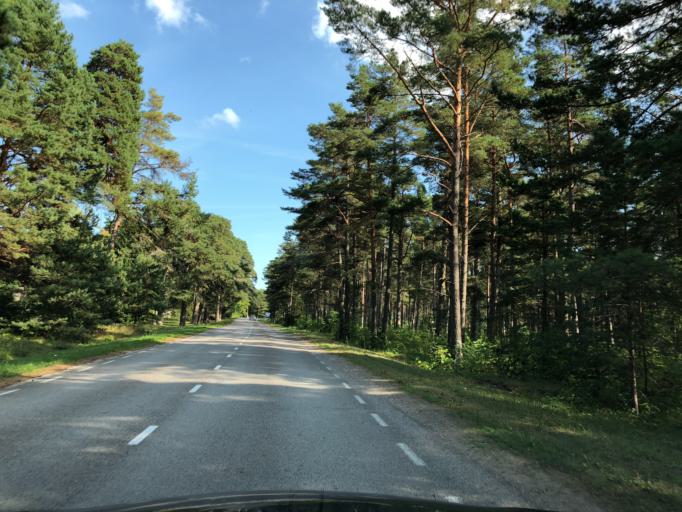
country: EE
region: Hiiumaa
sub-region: Kaerdla linn
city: Kardla
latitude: 58.7077
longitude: 22.5898
